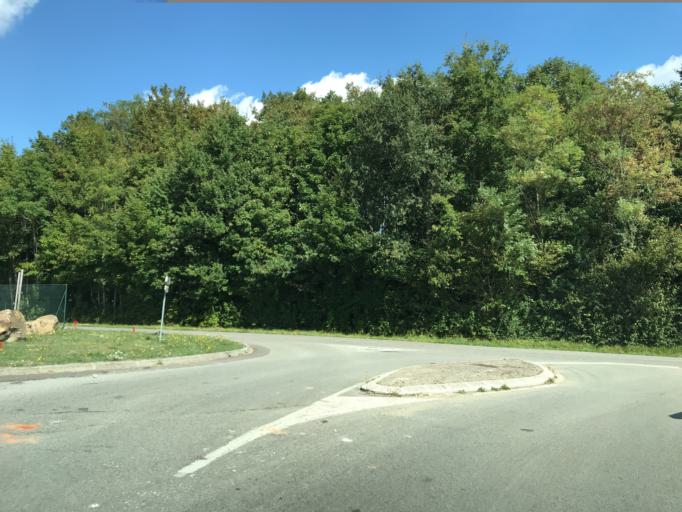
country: FR
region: Haute-Normandie
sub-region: Departement de l'Eure
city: La Chapelle-Reanville
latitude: 49.0948
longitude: 1.3912
